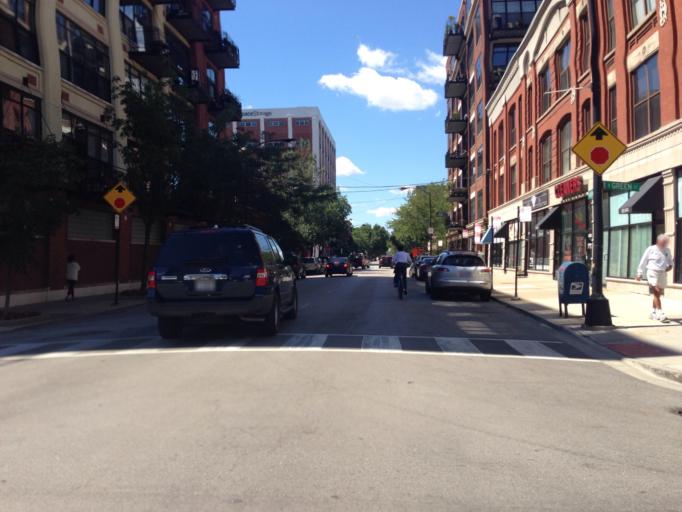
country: US
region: Illinois
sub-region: Cook County
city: Chicago
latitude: 41.8793
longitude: -87.6485
